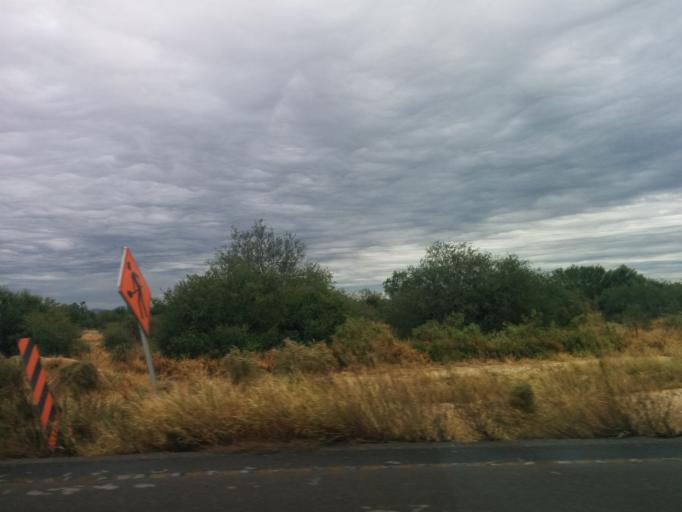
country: MX
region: Sonora
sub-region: San Miguel de Horcasitas
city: Las Mercedes [Agropecuaria]
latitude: 29.5326
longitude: -111.0089
